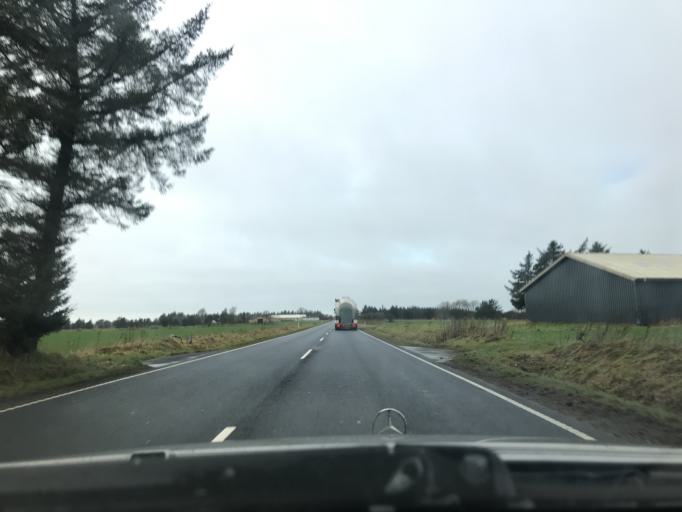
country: DK
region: South Denmark
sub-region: Esbjerg Kommune
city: Ribe
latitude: 55.2816
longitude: 8.8495
